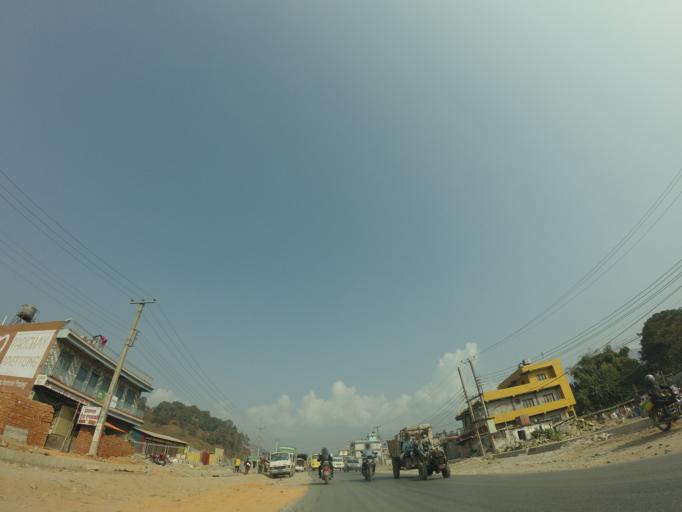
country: NP
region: Western Region
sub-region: Gandaki Zone
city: Pokhara
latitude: 28.2256
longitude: 83.9806
